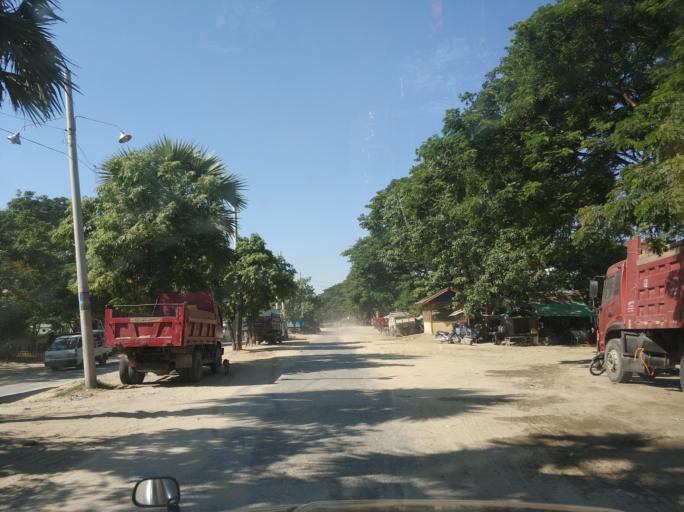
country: MM
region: Mandalay
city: Mandalay
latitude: 21.9585
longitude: 96.0526
